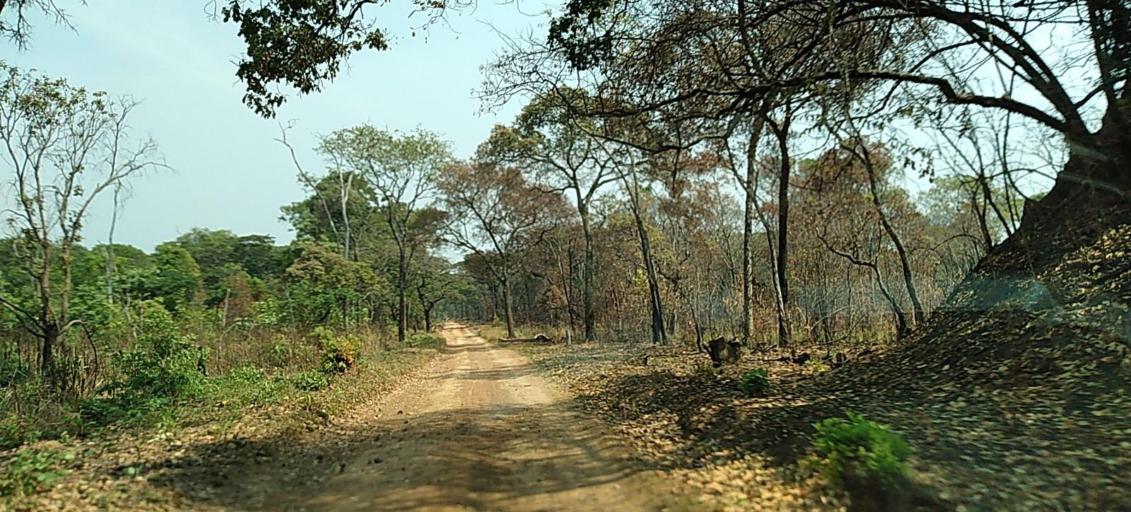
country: ZM
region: North-Western
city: Kansanshi
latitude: -12.0610
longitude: 26.8889
